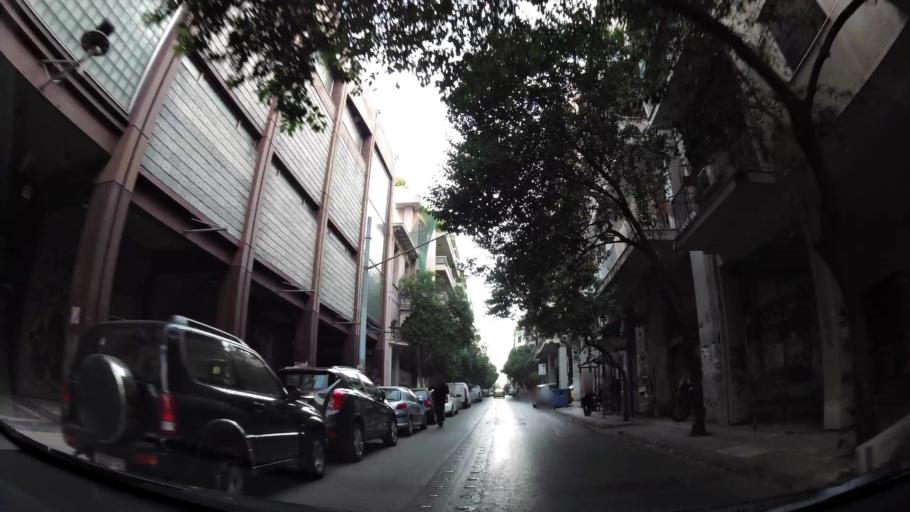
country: GR
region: Attica
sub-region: Nomarchia Athinas
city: Kipseli
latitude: 37.9869
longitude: 23.7411
